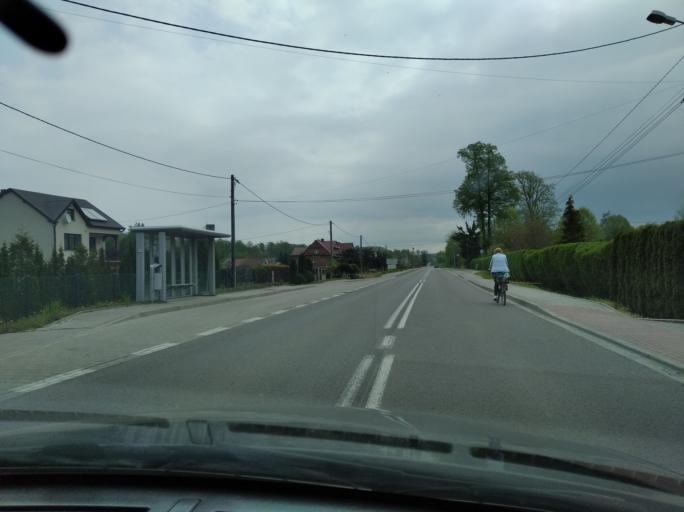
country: PL
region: Lesser Poland Voivodeship
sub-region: Powiat tarnowski
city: Skrzyszow
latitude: 49.9887
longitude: 21.0827
